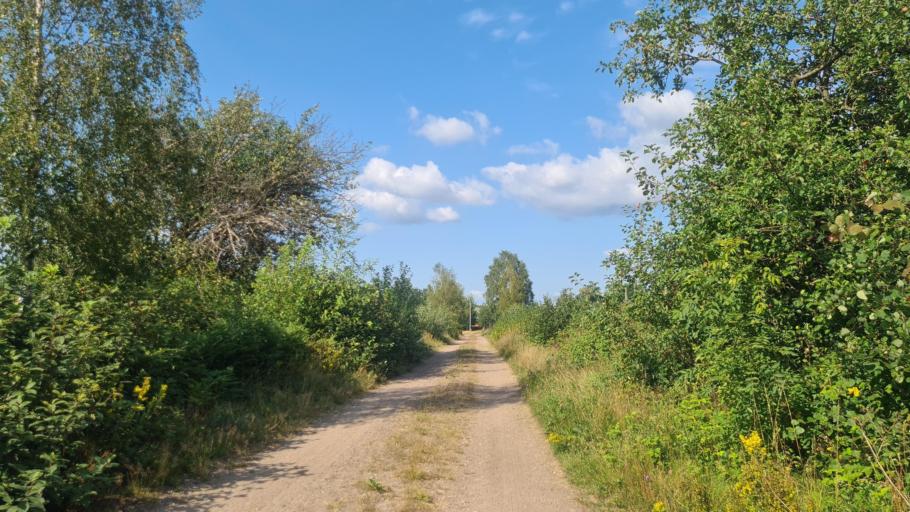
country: SE
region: Kronoberg
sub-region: Ljungby Kommun
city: Ljungby
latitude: 56.7752
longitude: 13.9014
